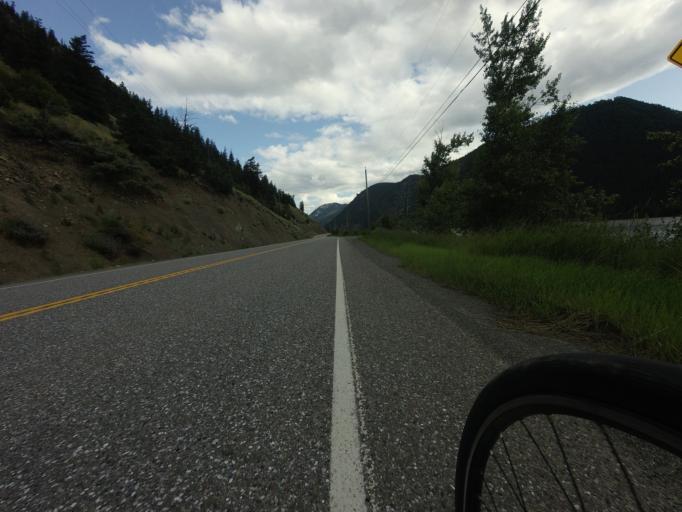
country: CA
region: British Columbia
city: Lillooet
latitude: 50.8702
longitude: -121.7385
